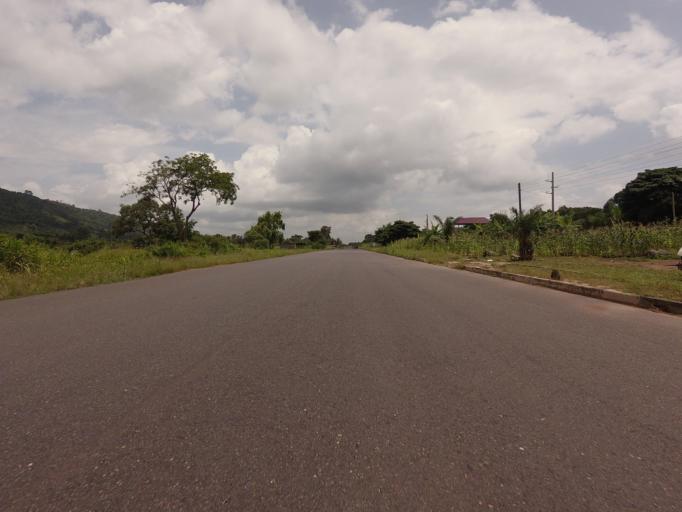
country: GH
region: Volta
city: Ho
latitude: 6.5062
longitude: 0.2105
